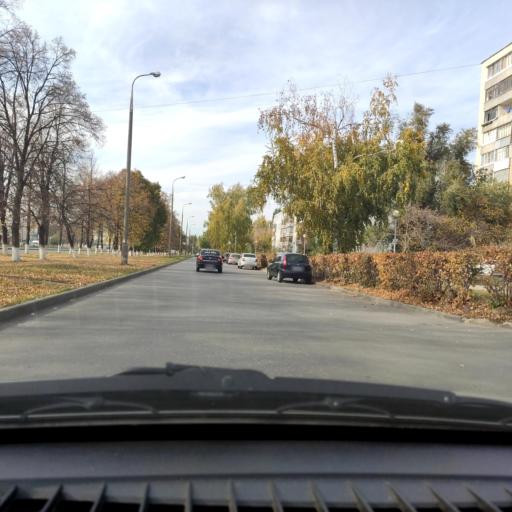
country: RU
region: Samara
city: Tol'yatti
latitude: 53.5303
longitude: 49.2699
